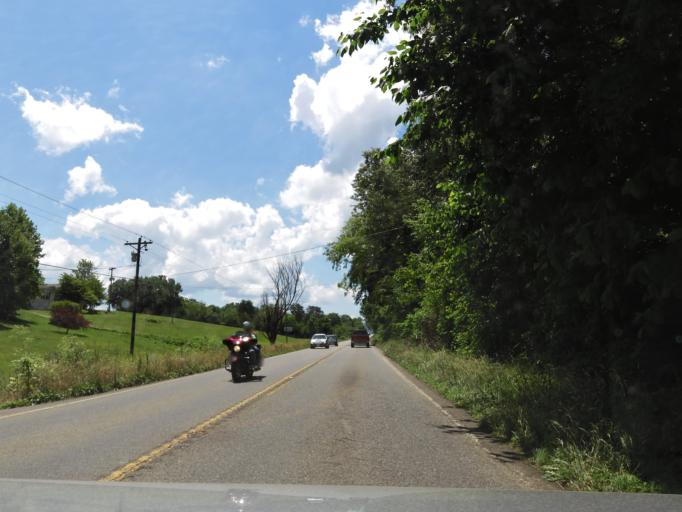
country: US
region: Tennessee
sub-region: Blount County
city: Maryville
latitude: 35.6944
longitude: -84.0428
